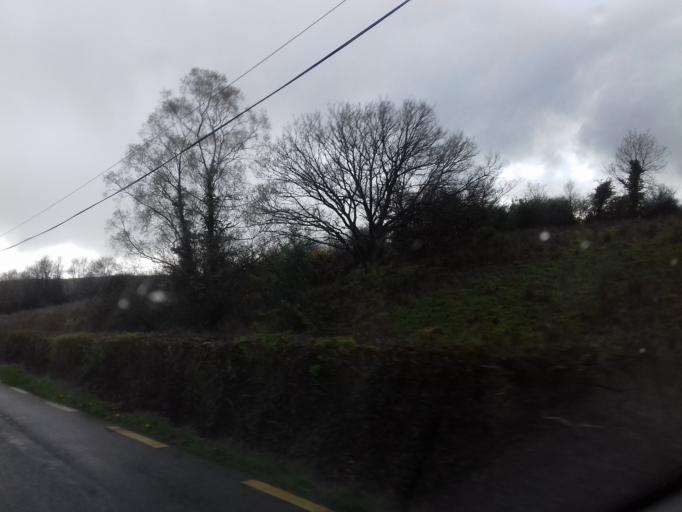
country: IE
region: Connaught
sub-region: County Leitrim
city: Manorhamilton
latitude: 54.2808
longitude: -7.9348
